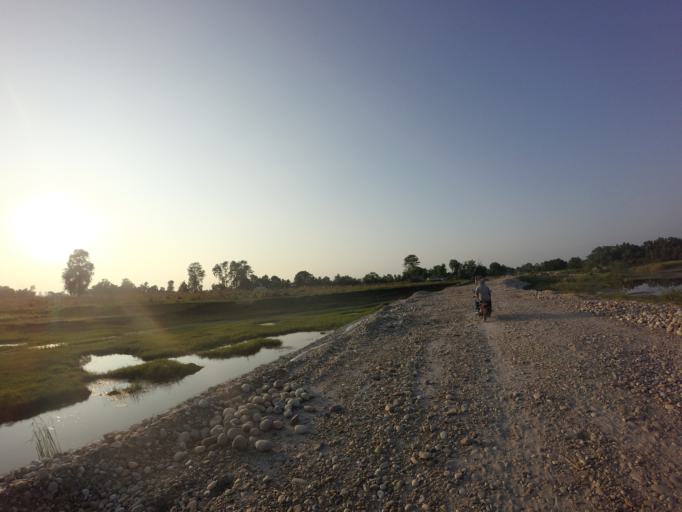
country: NP
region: Far Western
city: Tikapur
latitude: 28.4503
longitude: 81.0733
